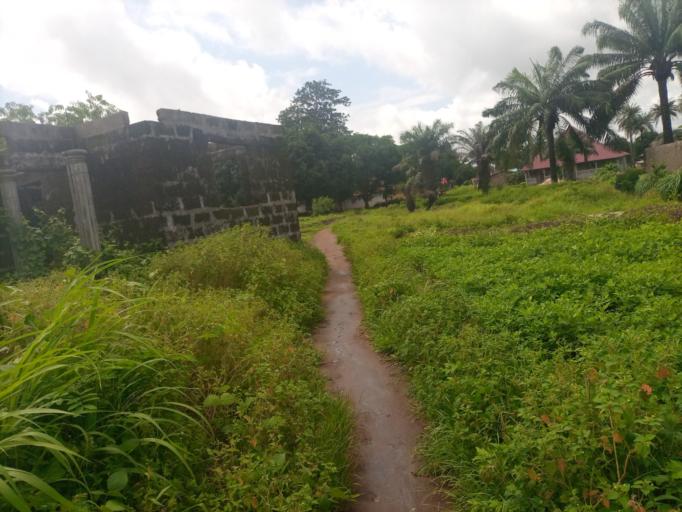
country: SL
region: Northern Province
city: Sawkta
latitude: 8.6332
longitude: -13.2093
